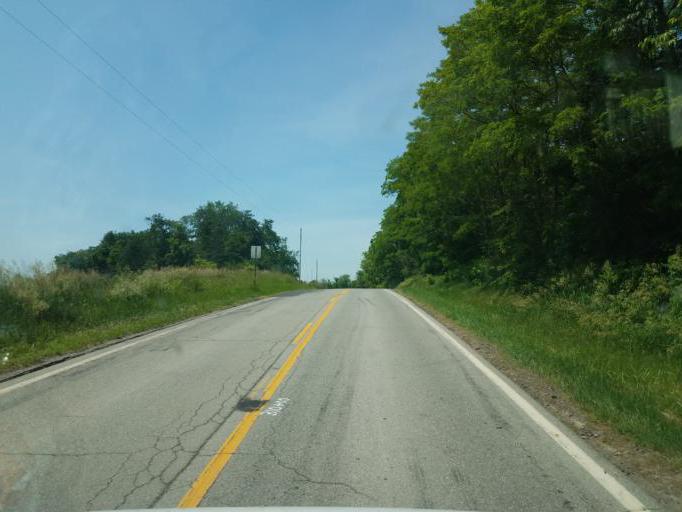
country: US
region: Ohio
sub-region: Ashland County
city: Loudonville
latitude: 40.7141
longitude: -82.2305
